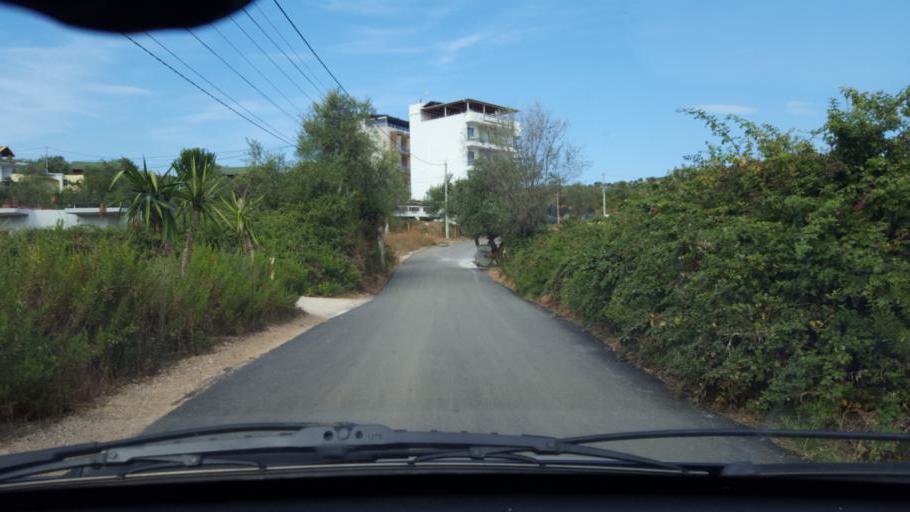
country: AL
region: Vlore
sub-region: Rrethi i Sarandes
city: Xarre
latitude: 39.7650
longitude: 19.9952
